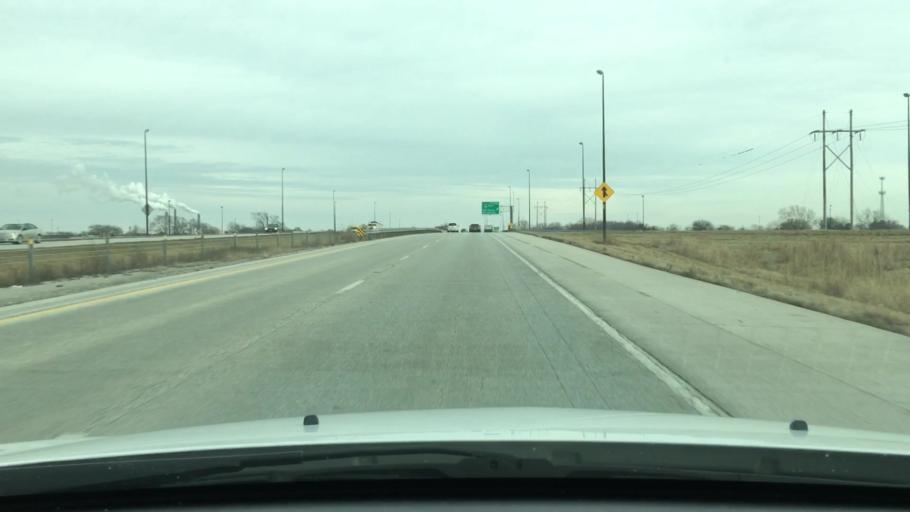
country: US
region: Illinois
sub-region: Sangamon County
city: Southern View
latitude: 39.7421
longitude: -89.6476
